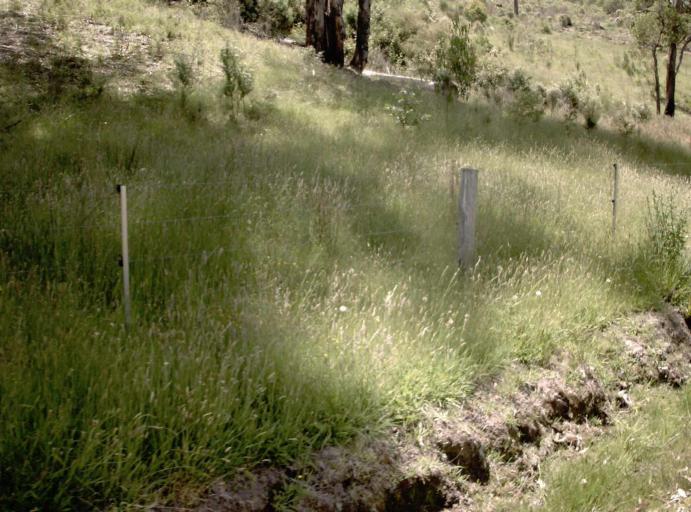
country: AU
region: New South Wales
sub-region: Bombala
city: Bombala
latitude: -37.3616
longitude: 149.0199
